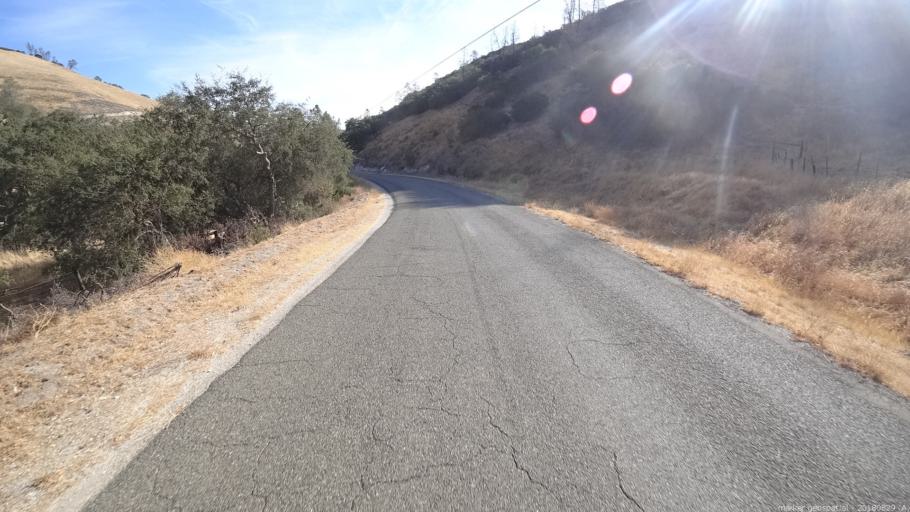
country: US
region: California
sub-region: Monterey County
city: King City
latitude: 35.9917
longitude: -121.0741
